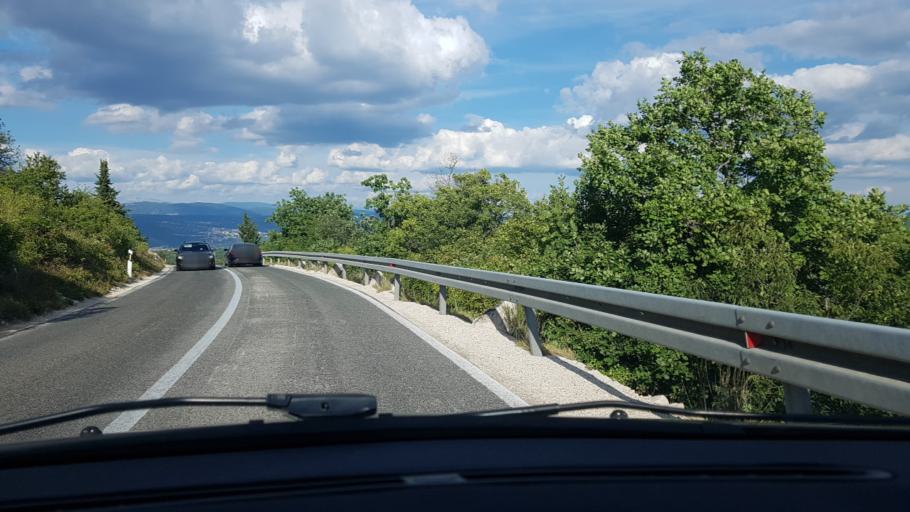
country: HR
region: Splitsko-Dalmatinska
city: Grubine
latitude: 43.4189
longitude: 17.1109
